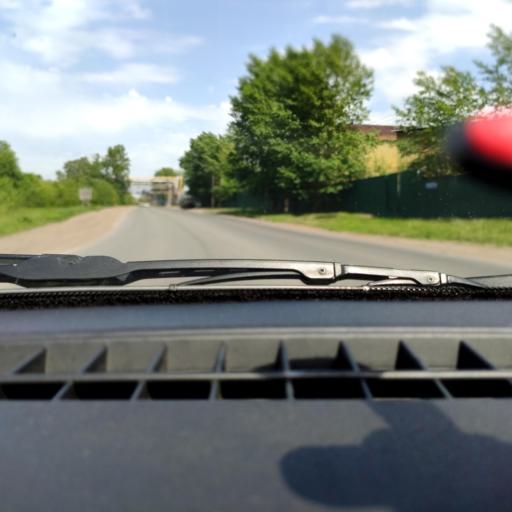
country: RU
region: Bashkortostan
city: Ufa
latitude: 54.8547
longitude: 56.0897
